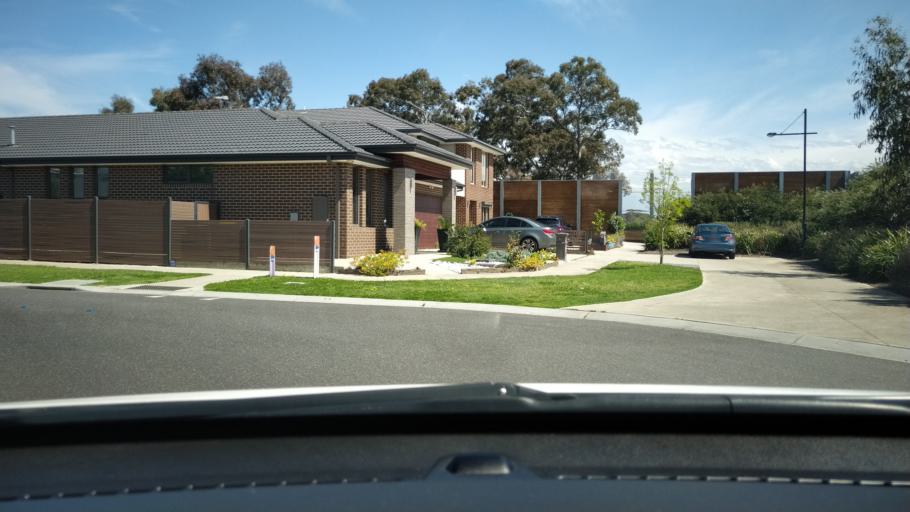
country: AU
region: Victoria
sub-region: Greater Dandenong
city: Keysborough
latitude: -37.9980
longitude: 145.1628
